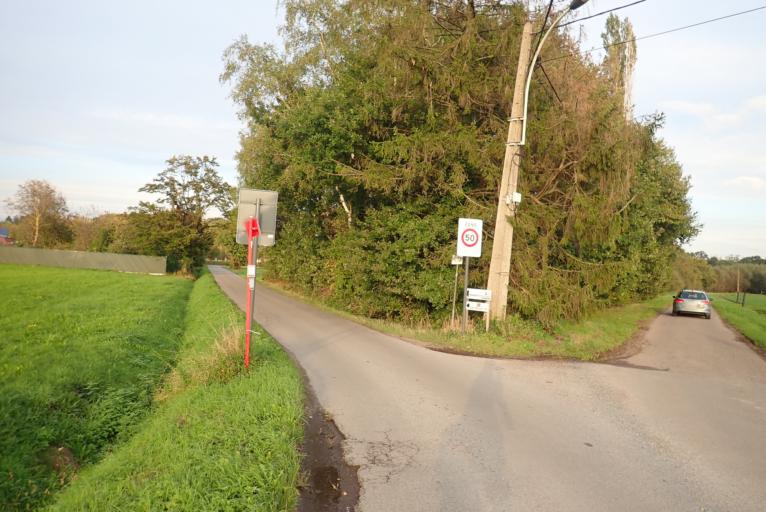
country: BE
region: Flanders
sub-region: Provincie Antwerpen
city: Zandhoven
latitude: 51.2031
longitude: 4.6479
